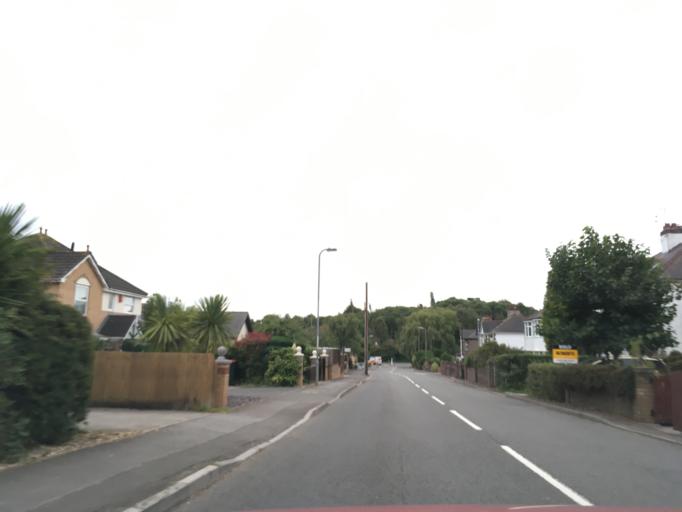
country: GB
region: Wales
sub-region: Newport
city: Langstone
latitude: 51.6049
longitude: -2.9106
